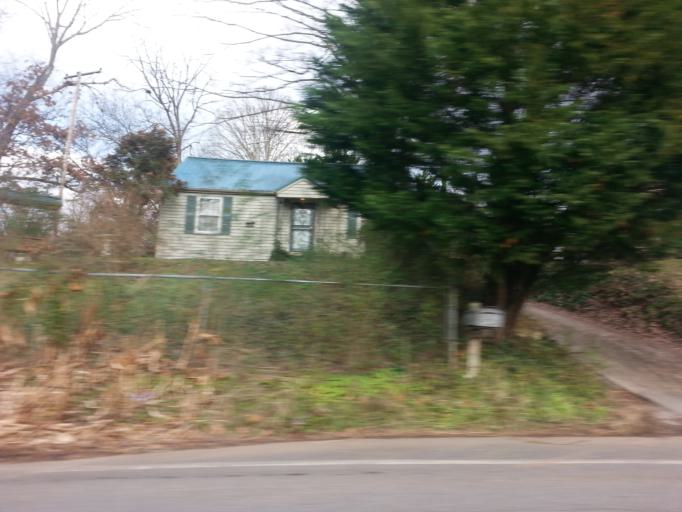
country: US
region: Tennessee
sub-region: Knox County
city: Knoxville
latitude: 35.9512
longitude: -83.8874
